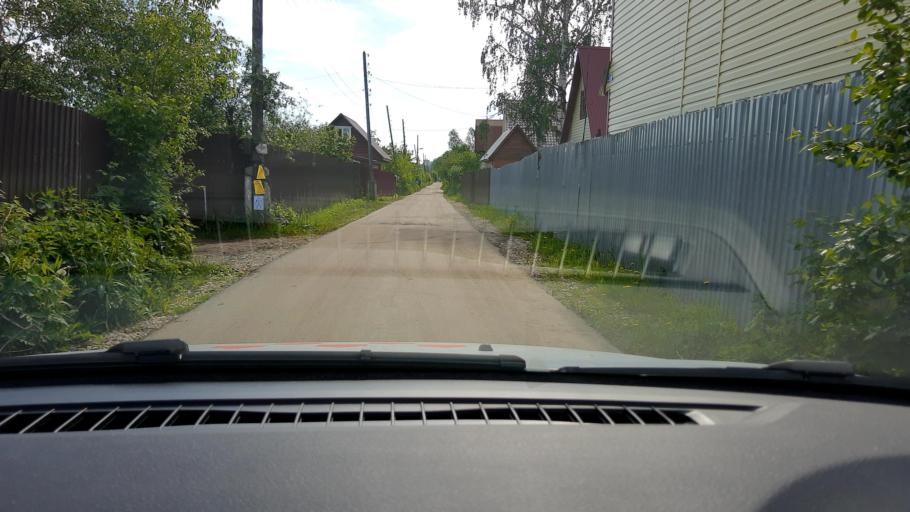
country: RU
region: Nizjnij Novgorod
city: Gorbatovka
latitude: 56.2599
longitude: 43.8283
